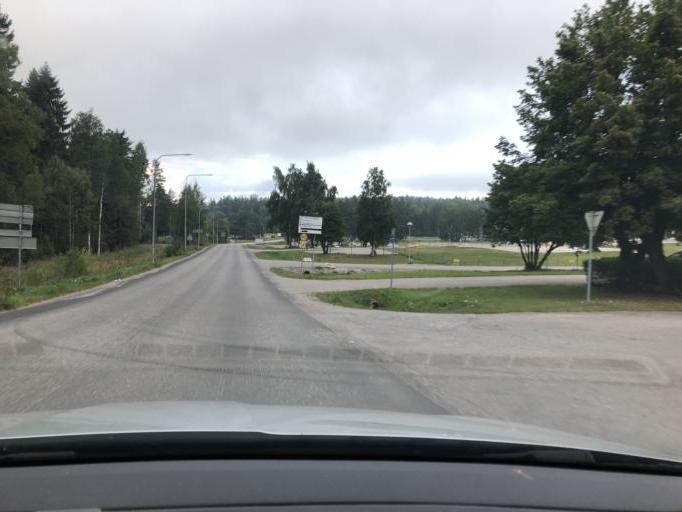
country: SE
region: Vaesternorrland
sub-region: Sundsvalls Kommun
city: Sundsvall
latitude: 62.4071
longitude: 17.3014
